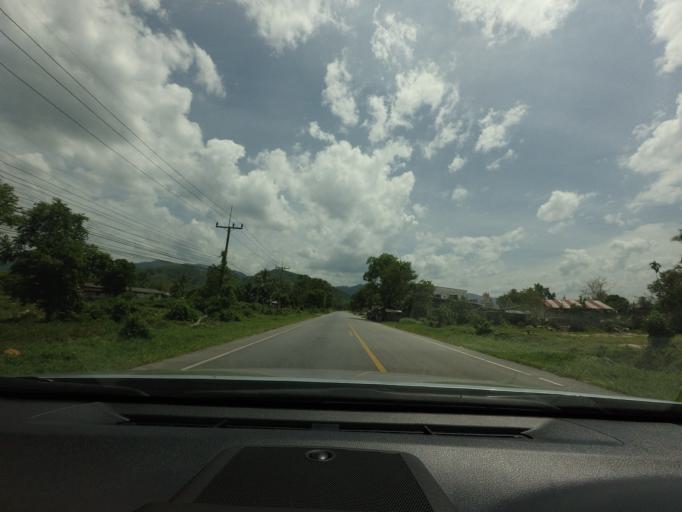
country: TH
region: Yala
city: Raman
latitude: 6.4553
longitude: 101.3555
